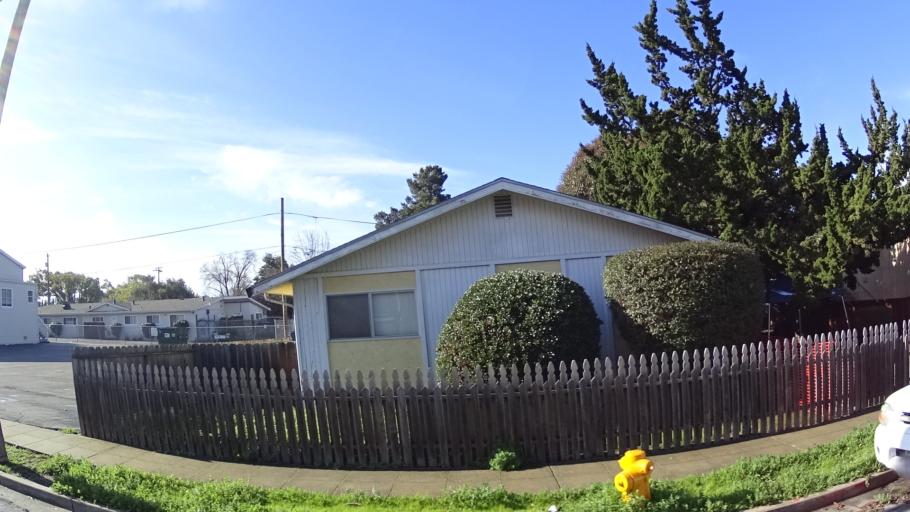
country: US
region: California
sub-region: Alameda County
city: Hayward
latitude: 37.6821
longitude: -122.0682
